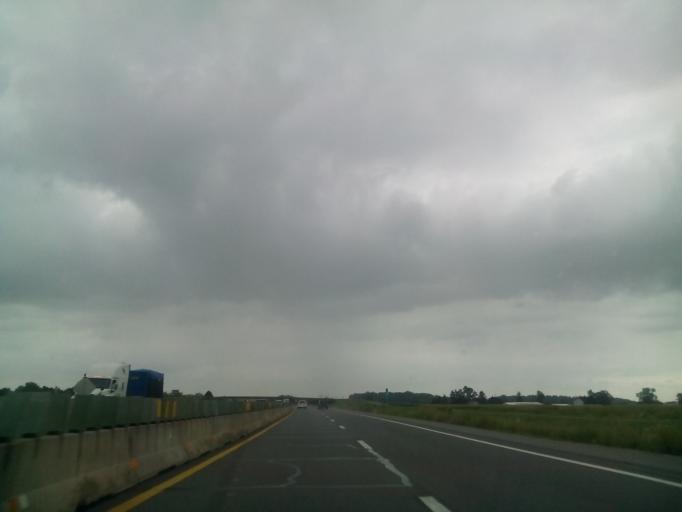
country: US
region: Ohio
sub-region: Sandusky County
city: Clyde
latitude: 41.3636
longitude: -82.9416
